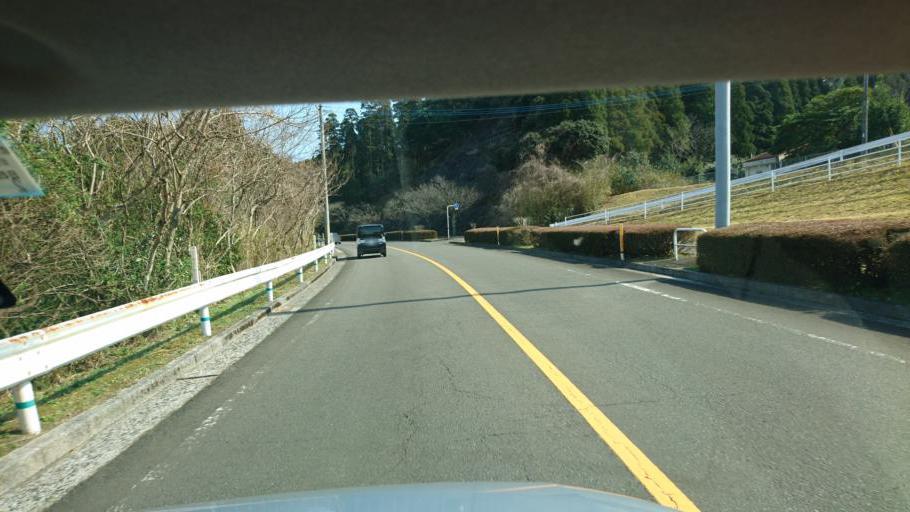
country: JP
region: Miyazaki
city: Miyazaki-shi
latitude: 31.8354
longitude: 131.4024
